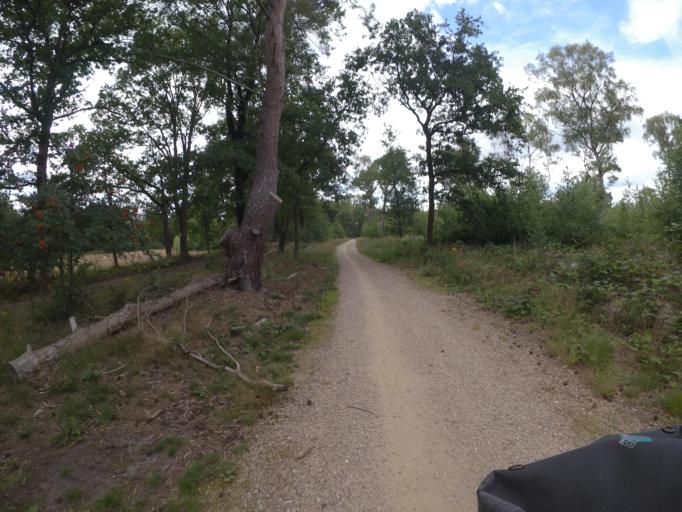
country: NL
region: North Brabant
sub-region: Gemeente Heeze-Leende
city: Heeze
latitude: 51.3940
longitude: 5.5913
